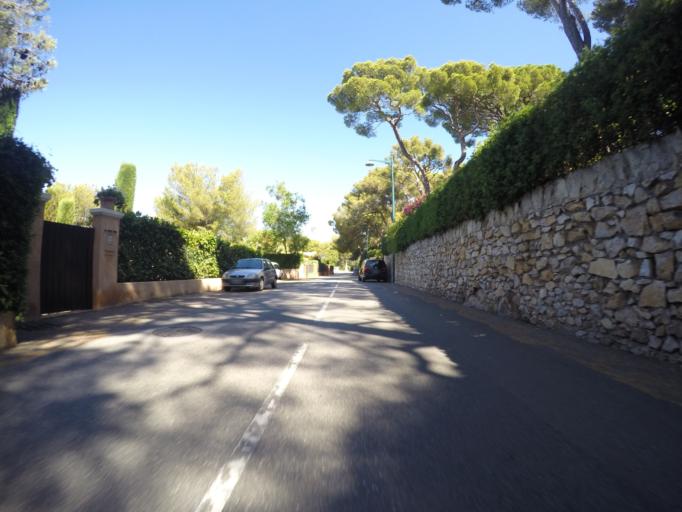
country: FR
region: Provence-Alpes-Cote d'Azur
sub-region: Departement des Alpes-Maritimes
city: Saint-Jean-Cap-Ferrat
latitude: 43.6869
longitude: 7.3244
